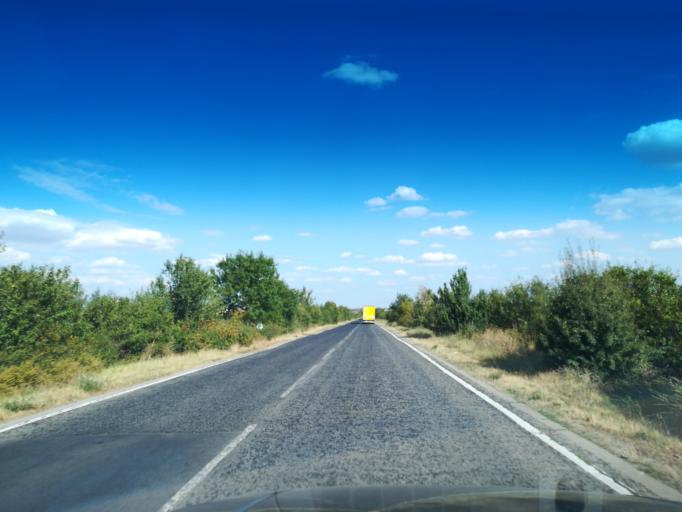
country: BG
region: Khaskovo
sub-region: Obshtina Mineralni Bani
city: Mineralni Bani
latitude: 42.0526
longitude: 25.3221
